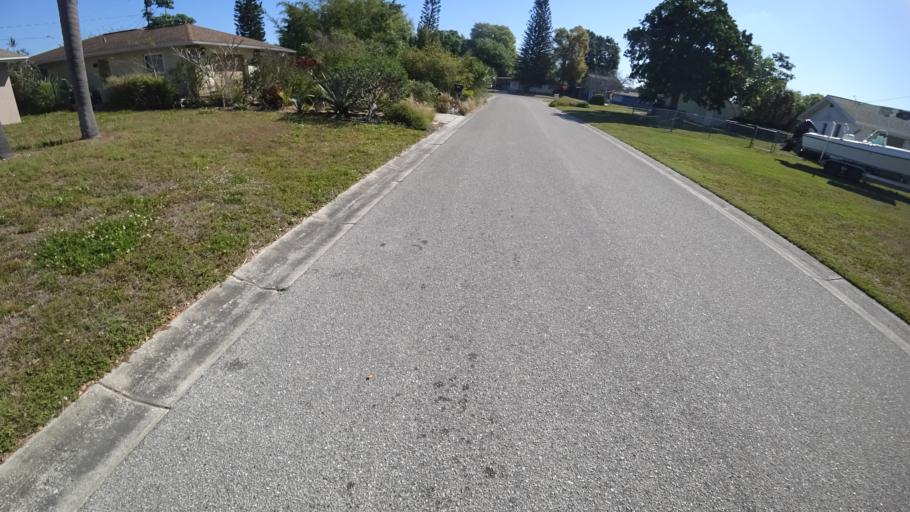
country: US
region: Florida
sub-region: Manatee County
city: Bayshore Gardens
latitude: 27.4293
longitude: -82.5930
